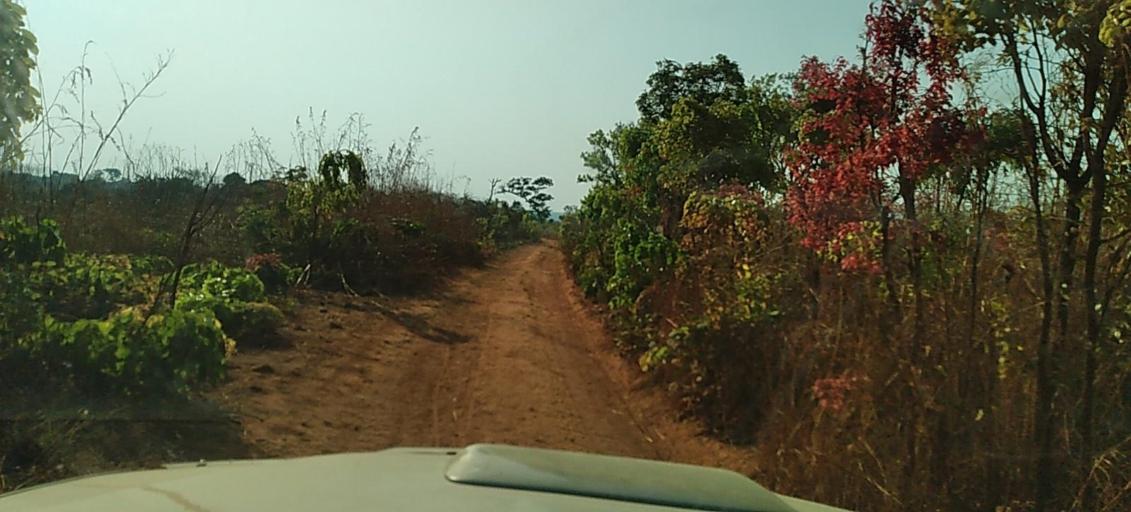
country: ZM
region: North-Western
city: Kasempa
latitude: -13.1831
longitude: 25.9497
